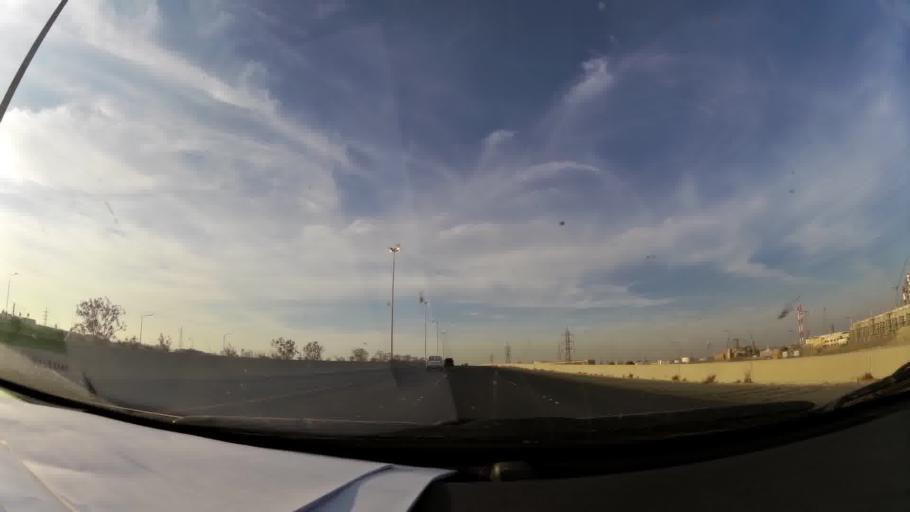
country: KW
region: Al Ahmadi
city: Al Fahahil
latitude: 28.9938
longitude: 48.1451
